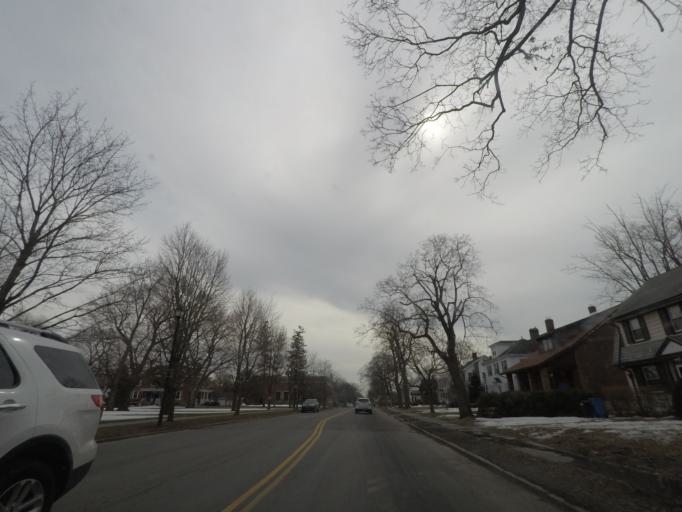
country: US
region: New York
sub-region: Albany County
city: Albany
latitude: 42.6527
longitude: -73.7850
